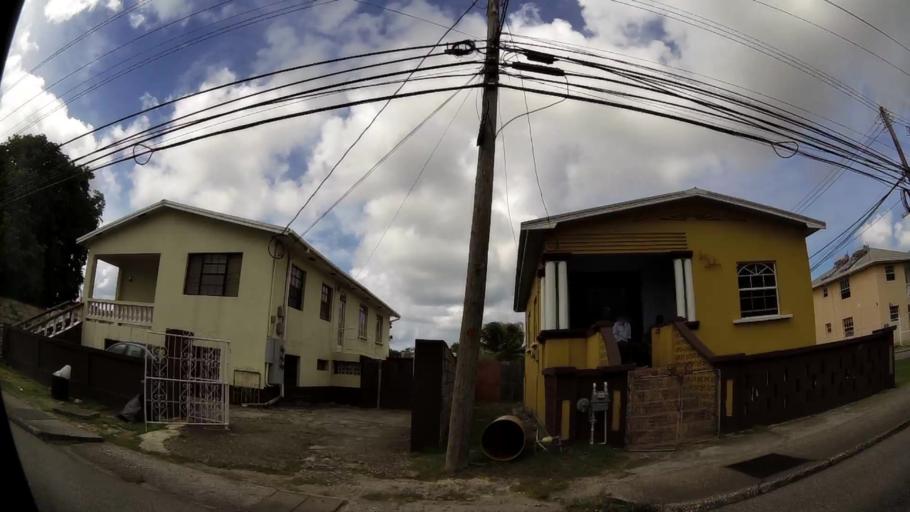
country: BB
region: Saint Michael
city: Bridgetown
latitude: 13.1221
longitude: -59.6095
